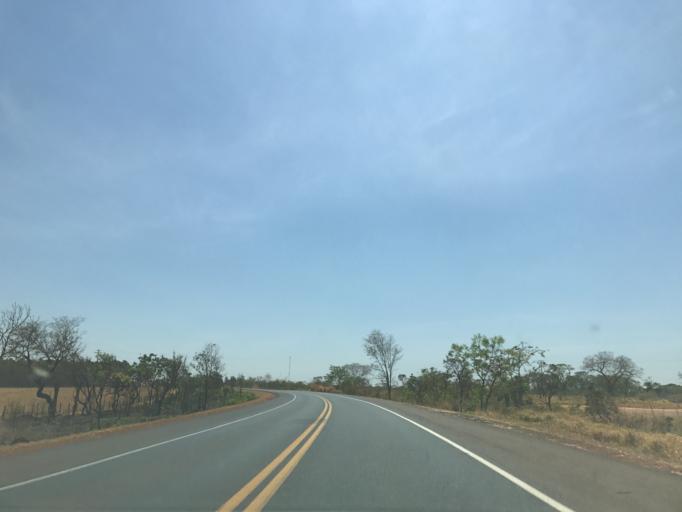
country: BR
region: Minas Gerais
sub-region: Frutal
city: Frutal
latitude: -19.8557
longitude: -48.9622
